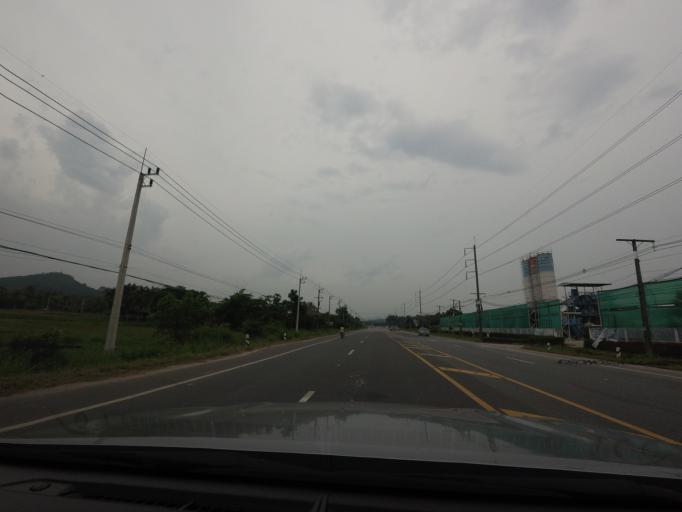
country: TH
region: Songkhla
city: Na Mom
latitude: 7.0469
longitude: 100.6537
